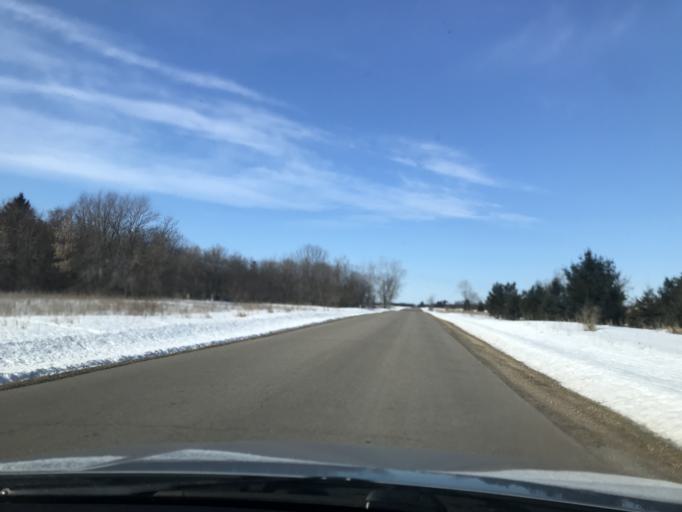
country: US
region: Wisconsin
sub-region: Oconto County
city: Oconto Falls
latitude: 44.9382
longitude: -88.1911
